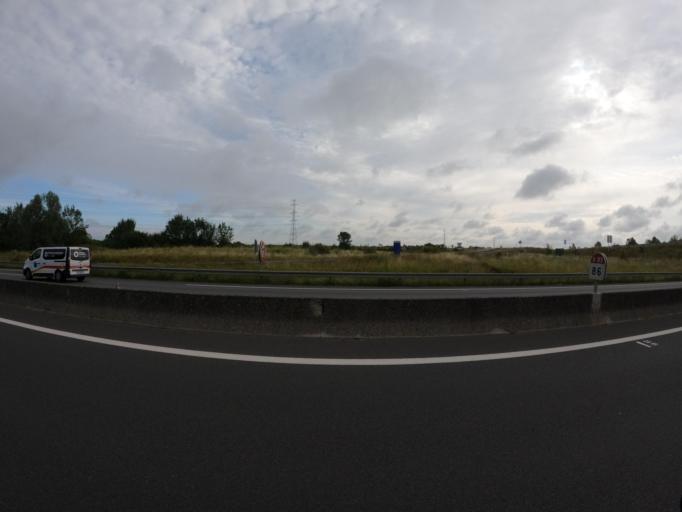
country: FR
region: Centre
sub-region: Departement d'Indre-et-Loire
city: Villandry
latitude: 47.3124
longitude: 0.5084
